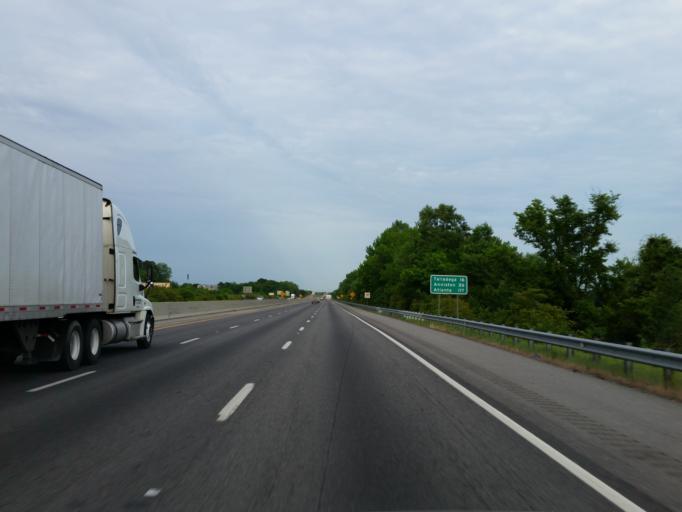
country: US
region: Alabama
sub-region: Saint Clair County
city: Riverside
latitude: 33.5953
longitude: -86.2005
